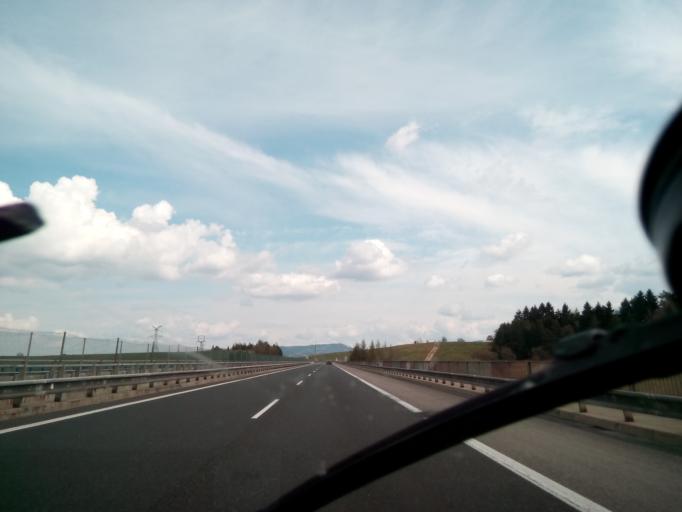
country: SK
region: Zilinsky
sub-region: Okres Liptovsky Mikulas
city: Pribylina
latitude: 49.0532
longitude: 19.7741
